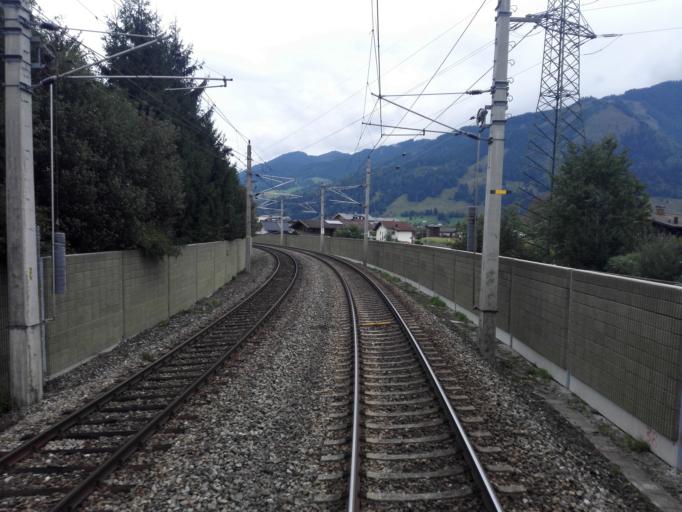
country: AT
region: Salzburg
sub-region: Politischer Bezirk Zell am See
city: Bruck an der Grossglocknerstrasse
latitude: 47.2846
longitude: 12.8175
